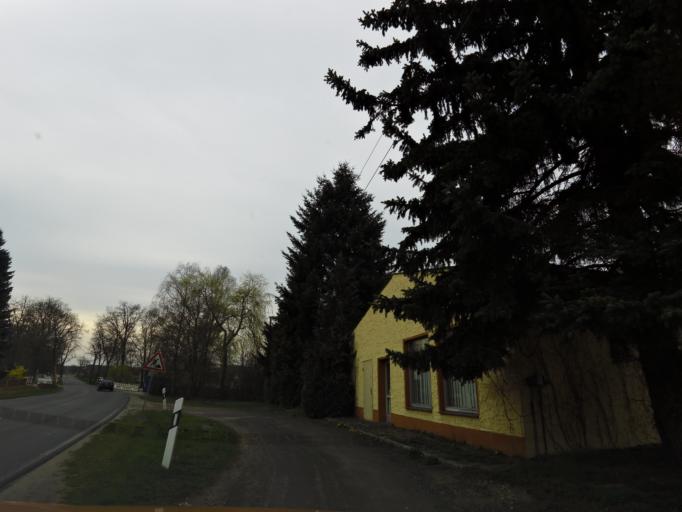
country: DE
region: Brandenburg
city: Tauche
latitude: 52.1723
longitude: 14.1992
